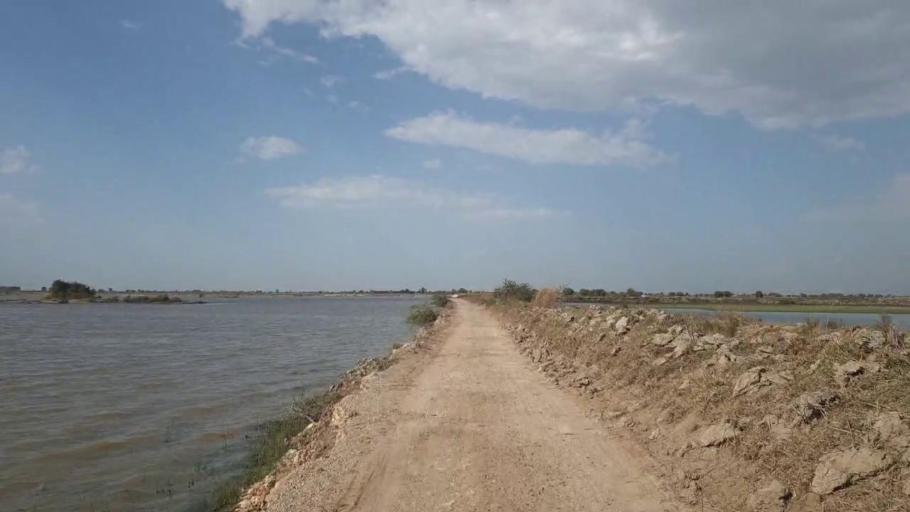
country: PK
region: Sindh
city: Shahdadpur
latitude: 25.9921
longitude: 68.4652
